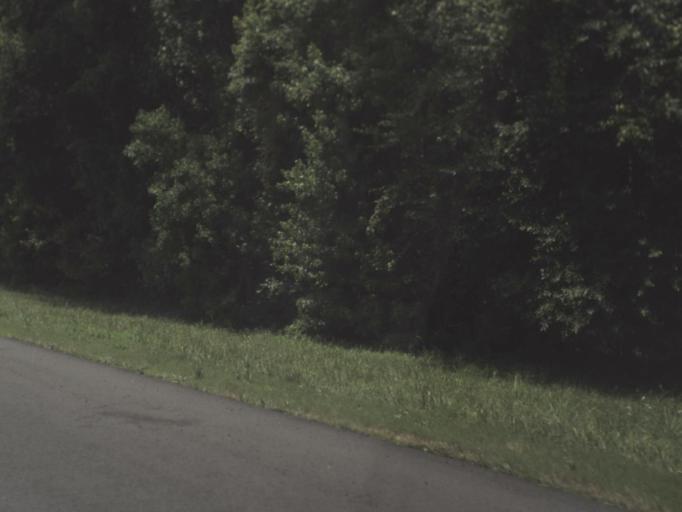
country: US
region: Florida
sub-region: Nassau County
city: Yulee
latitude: 30.6847
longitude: -81.6731
